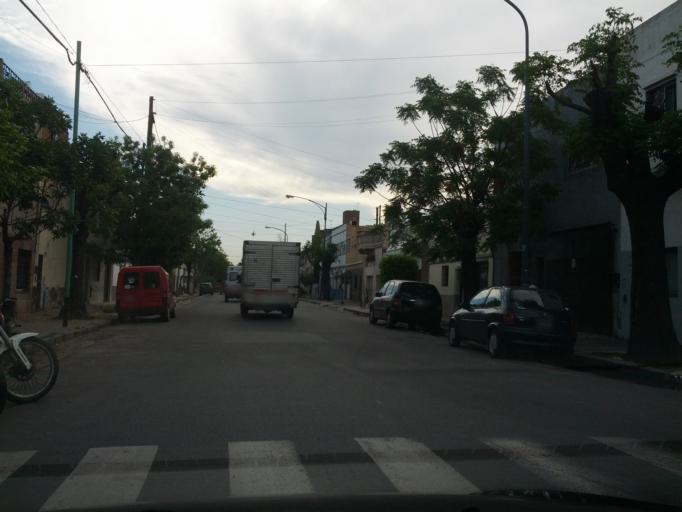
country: AR
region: Buenos Aires
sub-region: Partido de Avellaneda
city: Avellaneda
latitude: -34.6484
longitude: -58.4090
